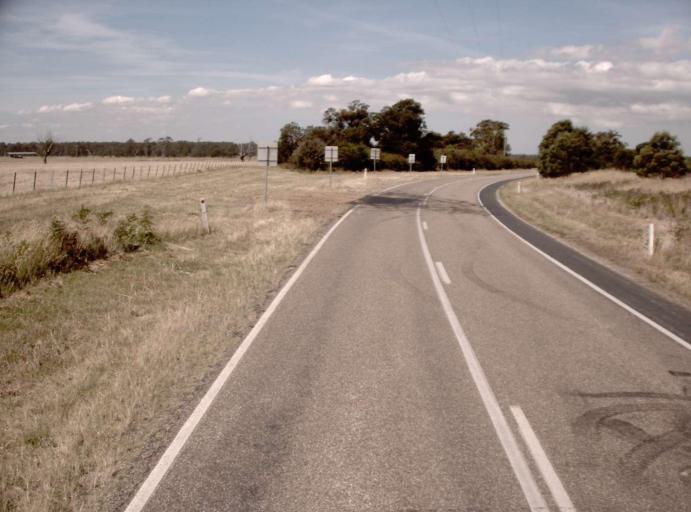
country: AU
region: Victoria
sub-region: Wellington
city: Sale
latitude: -38.1618
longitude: 146.9078
